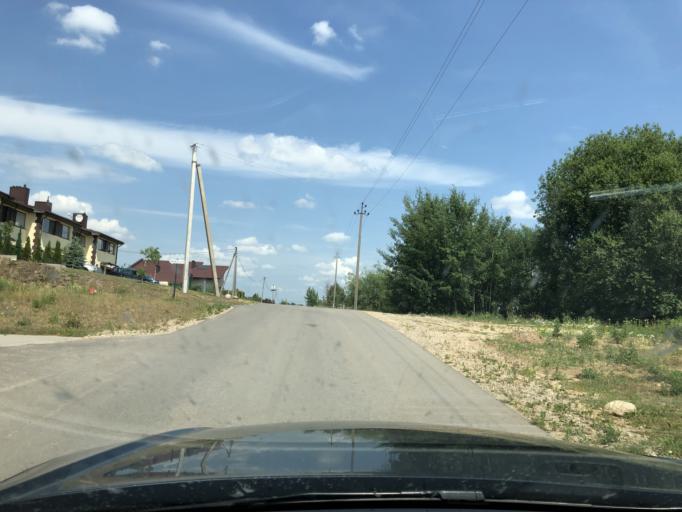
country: LT
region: Vilnius County
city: Pasilaiciai
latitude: 54.7516
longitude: 25.1912
